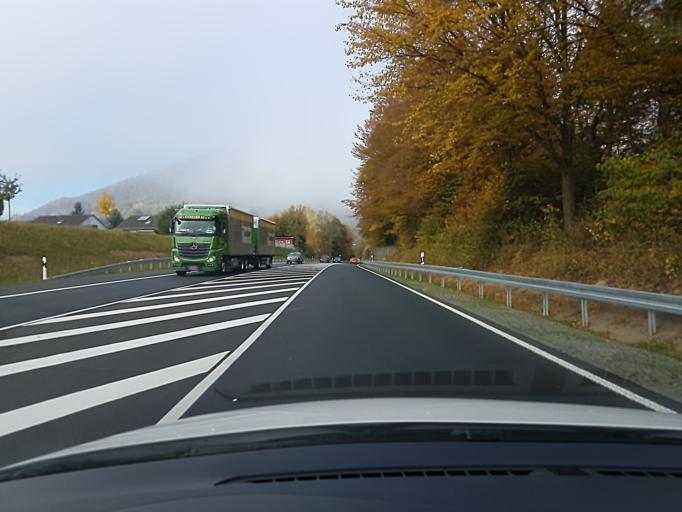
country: DE
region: Bavaria
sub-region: Regierungsbezirk Unterfranken
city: Kleinheubach
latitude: 49.7149
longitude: 9.2099
